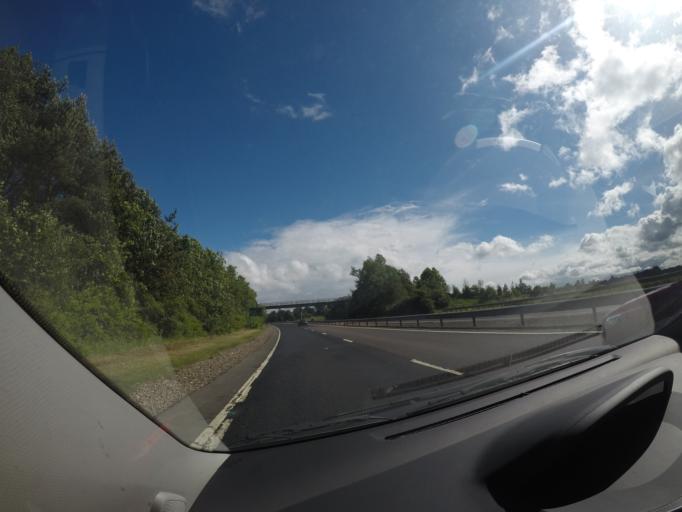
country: GB
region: Scotland
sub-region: Stirling
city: Dunblane
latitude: 56.1853
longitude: -3.9855
